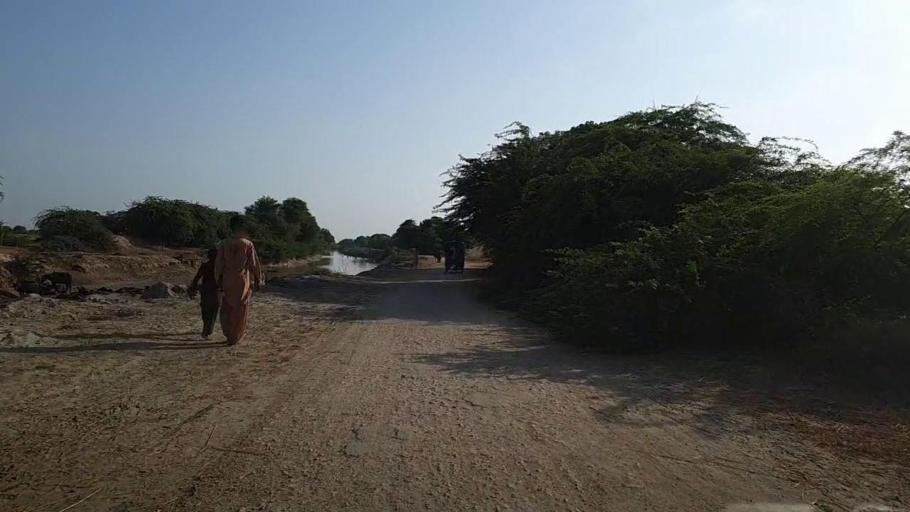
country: PK
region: Sindh
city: Kario
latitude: 24.7847
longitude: 68.6691
